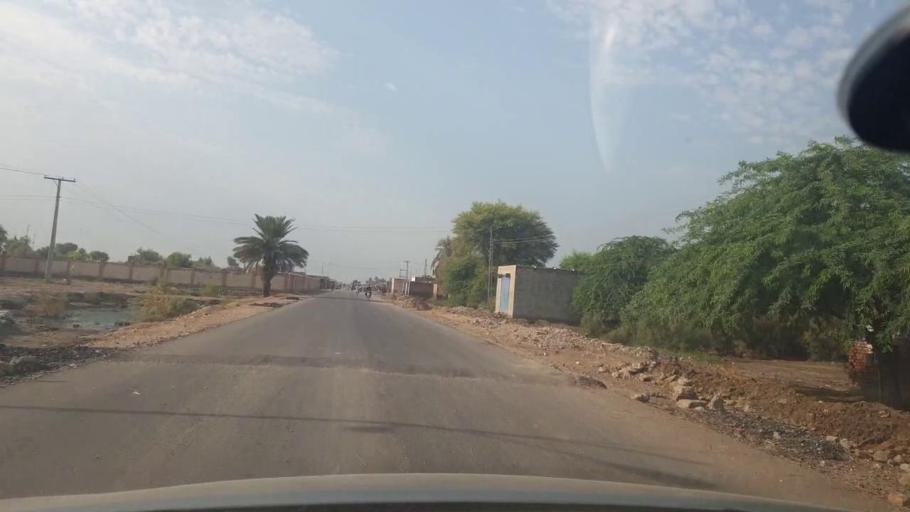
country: PK
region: Sindh
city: Jacobabad
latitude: 28.1077
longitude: 68.3262
